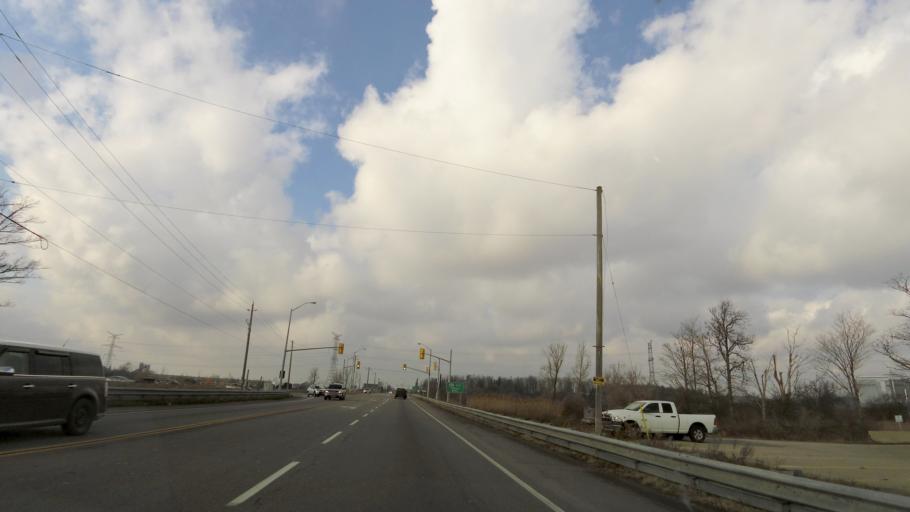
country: CA
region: Ontario
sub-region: Wellington County
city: Guelph
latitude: 43.4519
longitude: -80.1224
